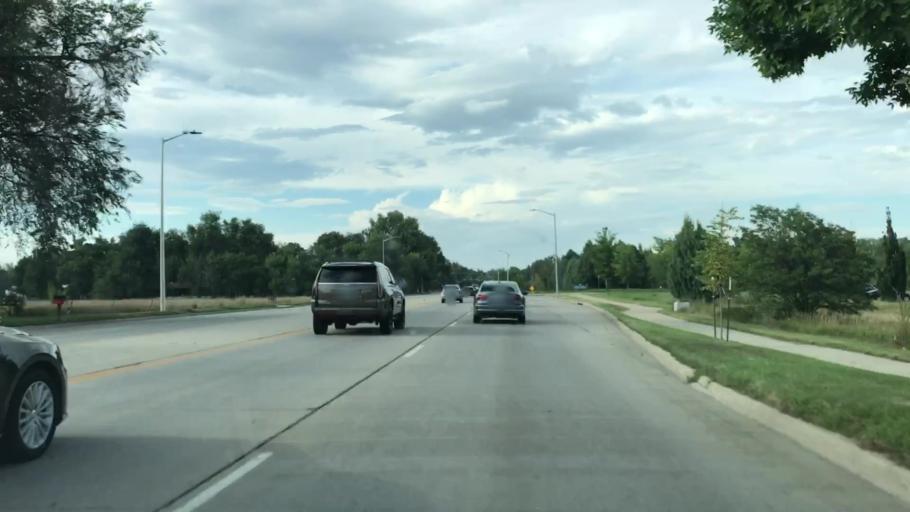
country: US
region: Colorado
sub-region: Boulder County
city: Longmont
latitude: 40.1625
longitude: -105.1306
